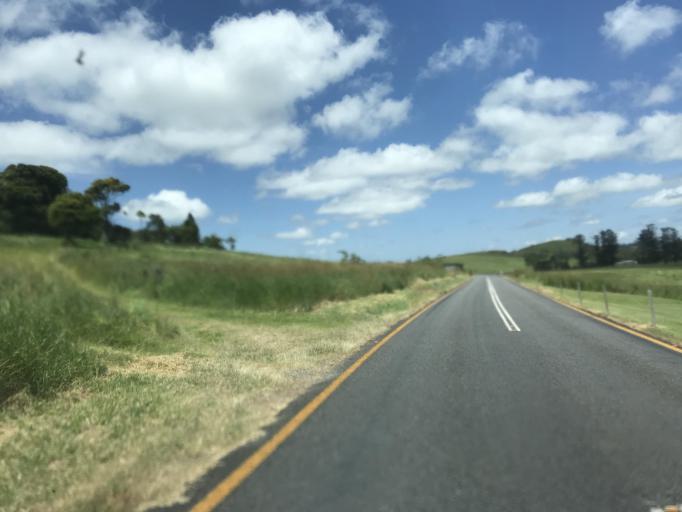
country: AU
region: Queensland
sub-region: Tablelands
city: Ravenshoe
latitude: -17.5252
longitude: 145.5450
